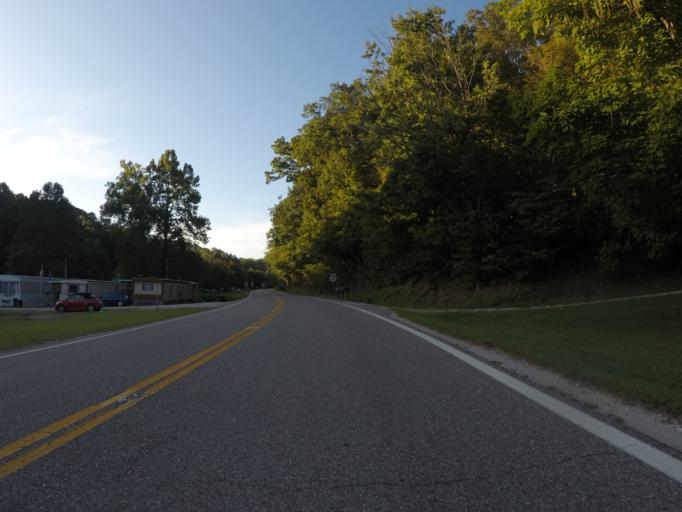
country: US
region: Ohio
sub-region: Lawrence County
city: Coal Grove
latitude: 38.5655
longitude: -82.5508
